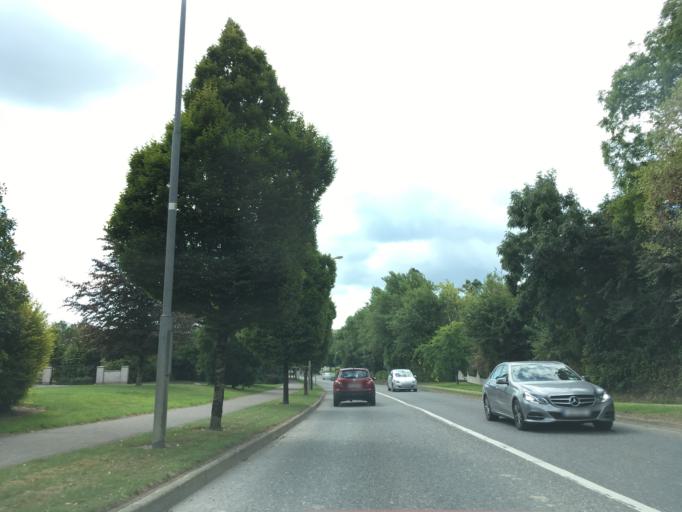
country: IE
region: Munster
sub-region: County Cork
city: Carrigaline
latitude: 51.8236
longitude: -8.3936
